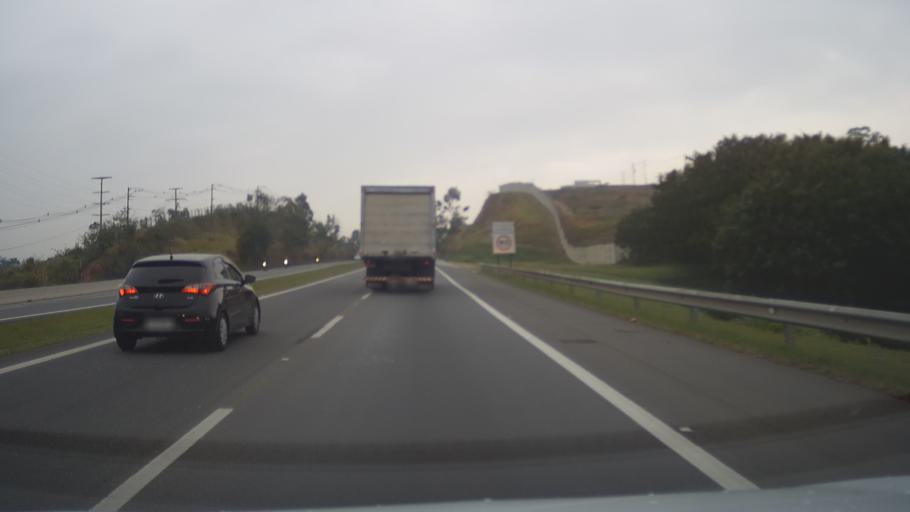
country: BR
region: Sao Paulo
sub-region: Jundiai
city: Jundiai
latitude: -23.1586
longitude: -46.8969
